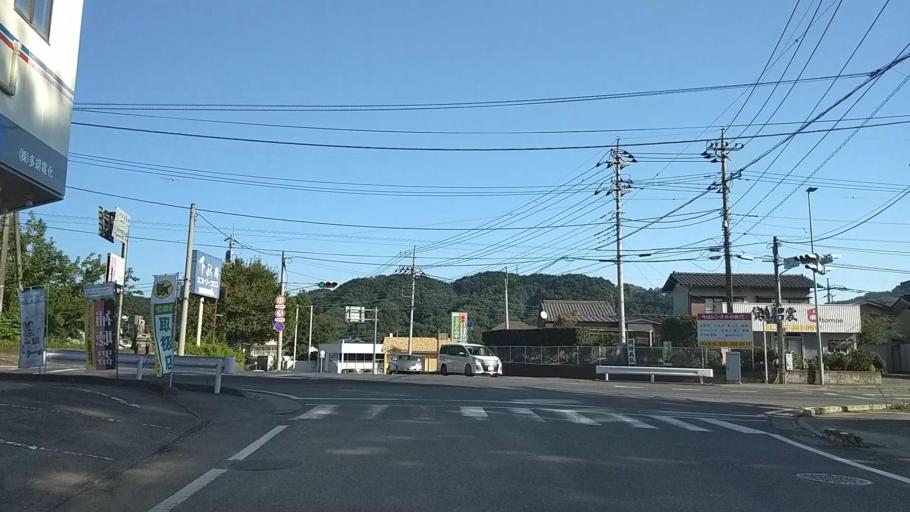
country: JP
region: Gunma
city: Annaka
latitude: 36.3329
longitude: 138.9007
